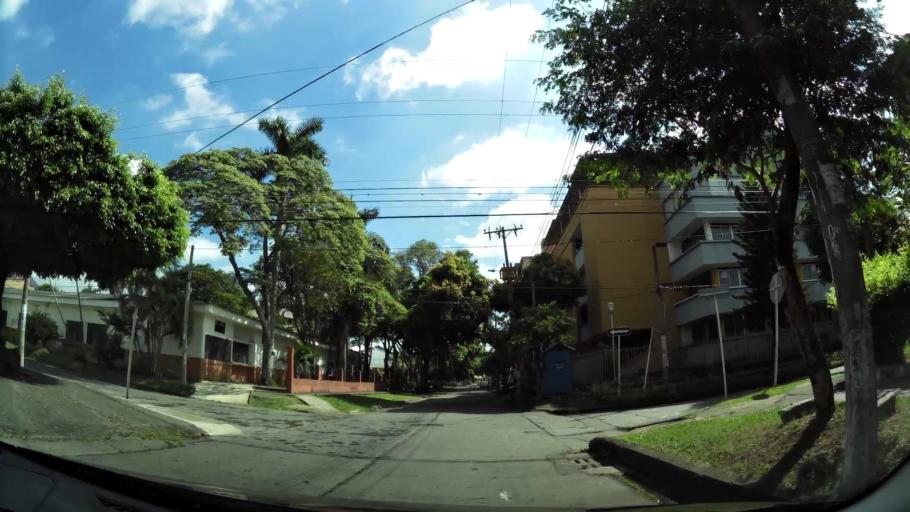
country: CO
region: Valle del Cauca
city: Cali
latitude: 3.4311
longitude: -76.5404
